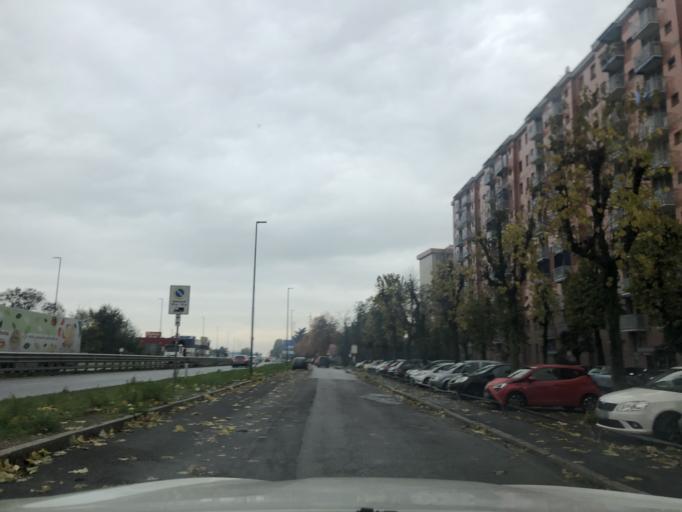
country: IT
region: Lombardy
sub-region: Citta metropolitana di Milano
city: Cesano Boscone
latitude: 45.4356
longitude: 9.0961
